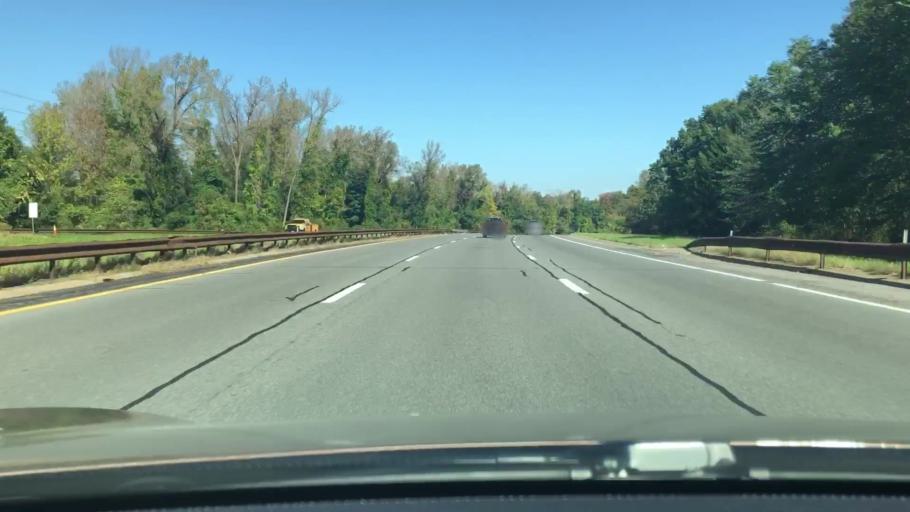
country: US
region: New York
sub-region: Westchester County
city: Greenburgh
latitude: 41.0283
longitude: -73.8207
